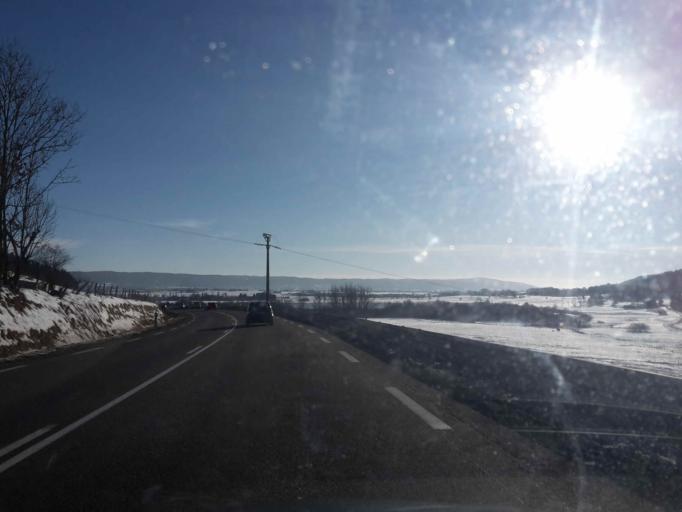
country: FR
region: Franche-Comte
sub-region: Departement du Doubs
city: Doubs
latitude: 46.9583
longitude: 6.3417
